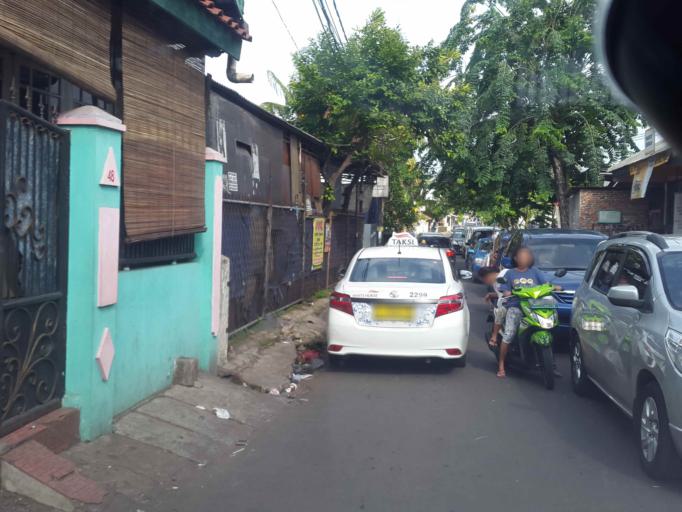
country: ID
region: West Java
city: Bekasi
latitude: -6.2768
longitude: 106.9130
